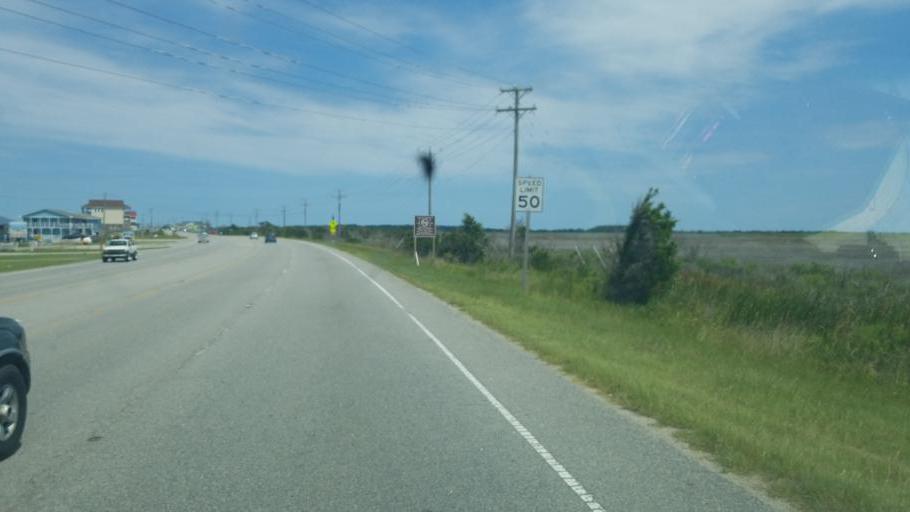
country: US
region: North Carolina
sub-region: Dare County
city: Manteo
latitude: 35.8964
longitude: -75.6208
